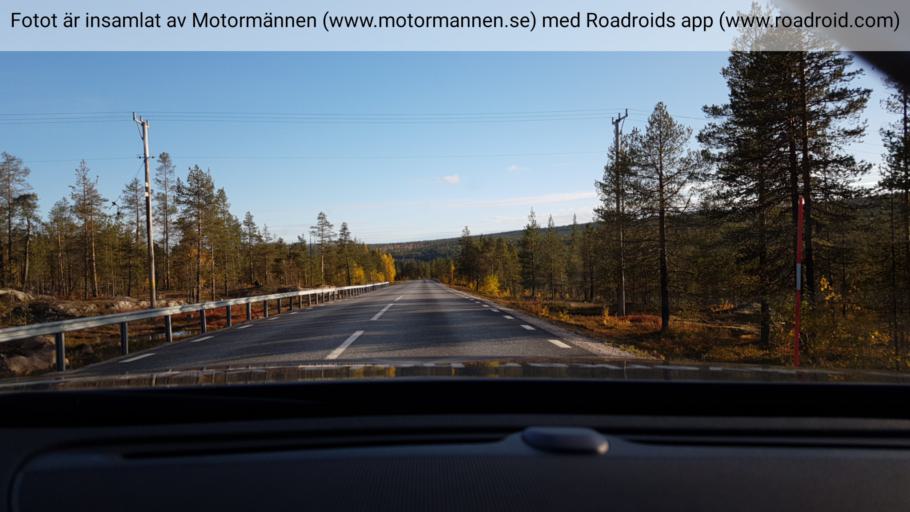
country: SE
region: Norrbotten
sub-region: Jokkmokks Kommun
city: Jokkmokk
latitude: 66.8611
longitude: 19.8182
